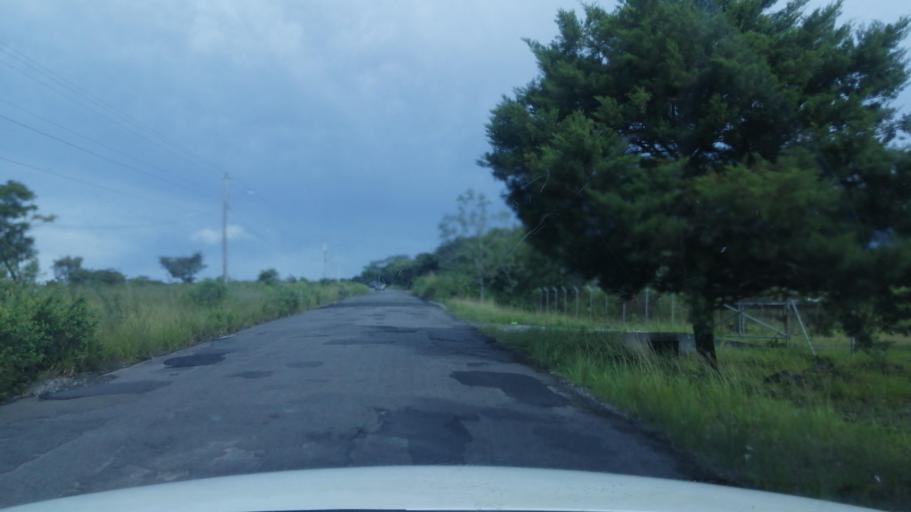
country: PA
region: Chiriqui
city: Potrerillos Abajo
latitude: 8.6702
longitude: -82.4336
